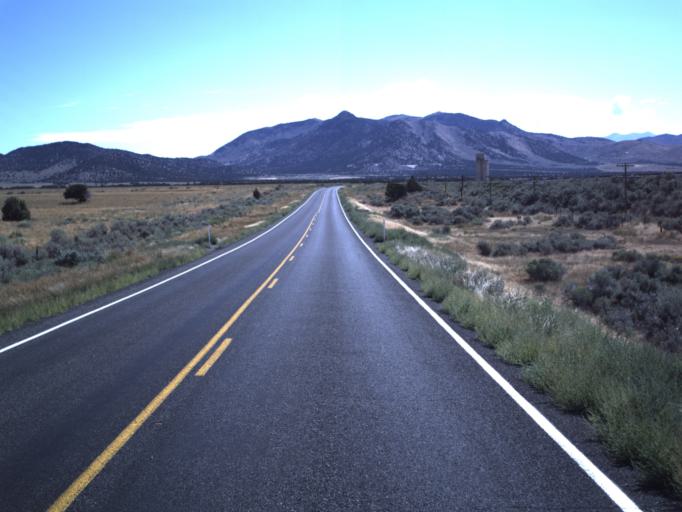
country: US
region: Utah
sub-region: Utah County
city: Genola
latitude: 39.9442
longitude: -112.2055
